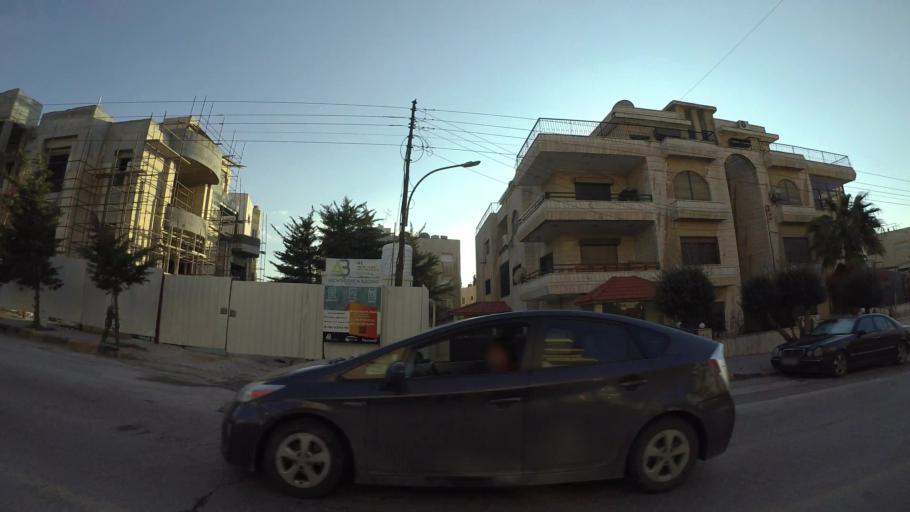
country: JO
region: Amman
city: Al Jubayhah
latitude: 31.9749
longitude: 35.8732
